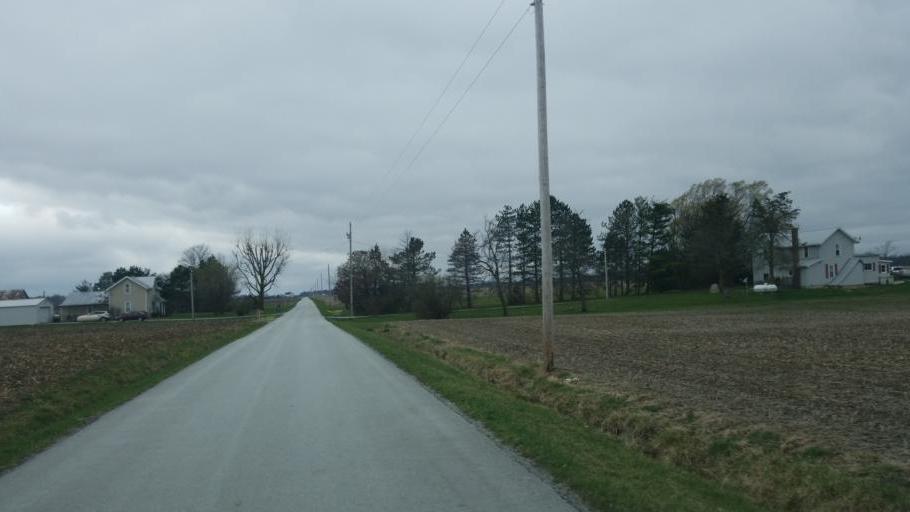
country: US
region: Ohio
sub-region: Hardin County
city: Forest
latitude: 40.7236
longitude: -83.5053
